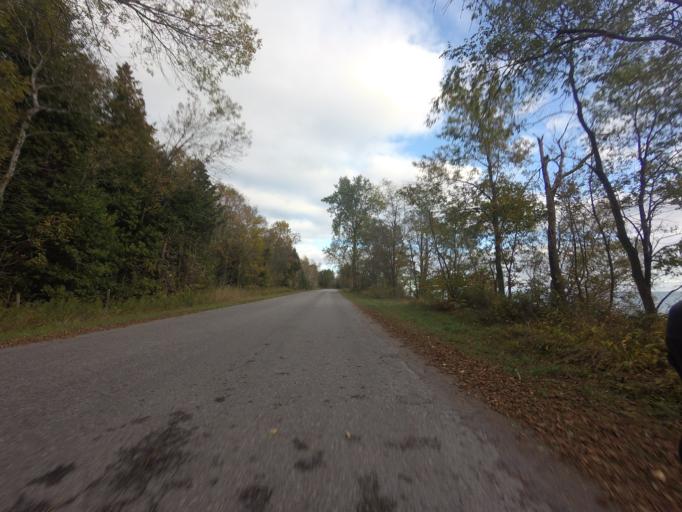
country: CA
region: Ontario
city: Cobourg
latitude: 43.9773
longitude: -77.9664
